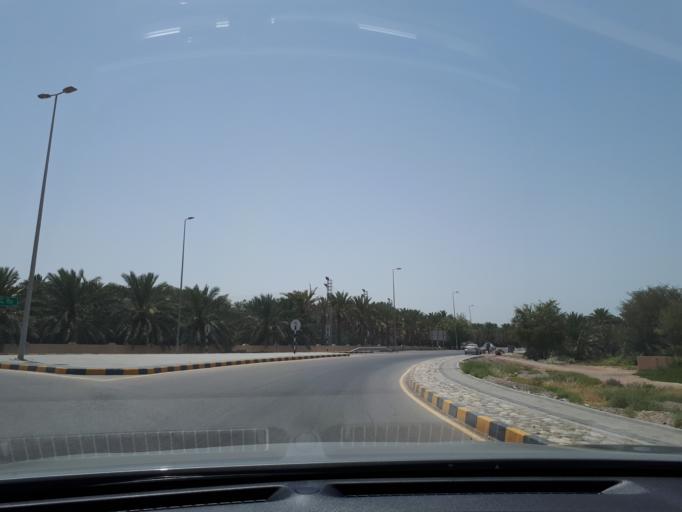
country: OM
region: Muhafazat Masqat
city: As Sib al Jadidah
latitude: 23.6793
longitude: 58.1384
